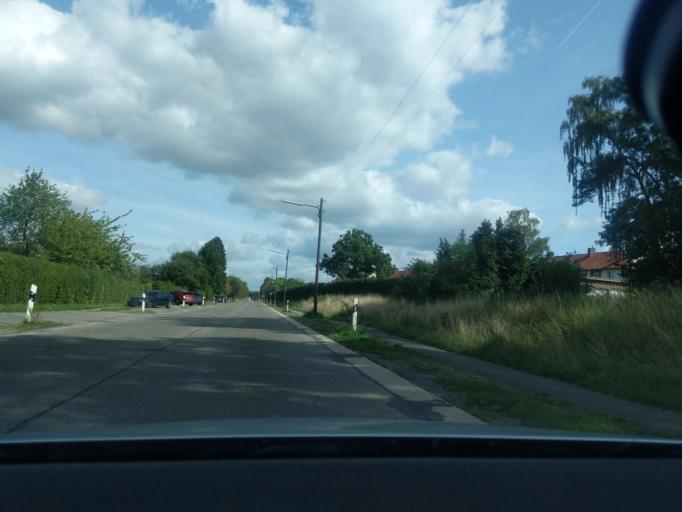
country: DE
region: Lower Saxony
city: Osnabrueck
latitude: 52.2978
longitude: 8.0426
